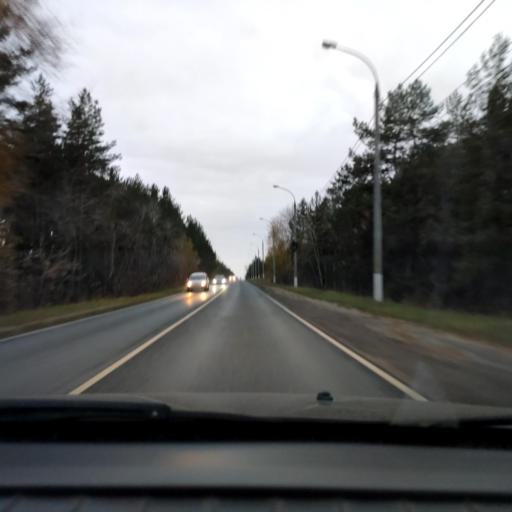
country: RU
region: Samara
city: Zhigulevsk
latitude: 53.4782
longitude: 49.4359
